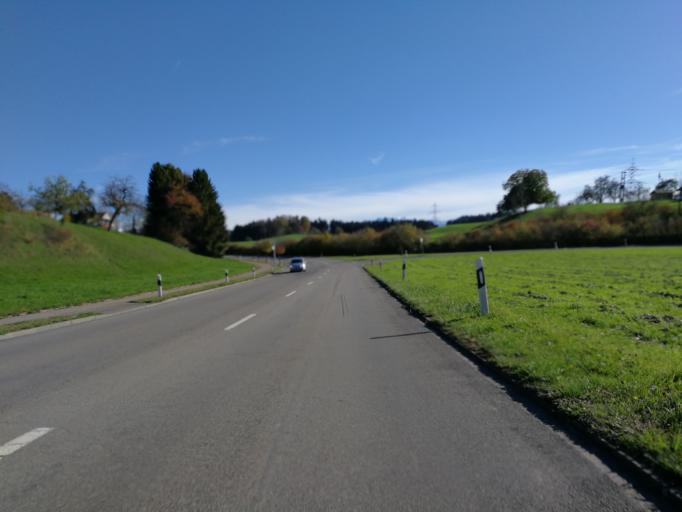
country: CH
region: Zurich
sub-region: Bezirk Uster
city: Moenchaltorf / Dorf
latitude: 47.2892
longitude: 8.7349
